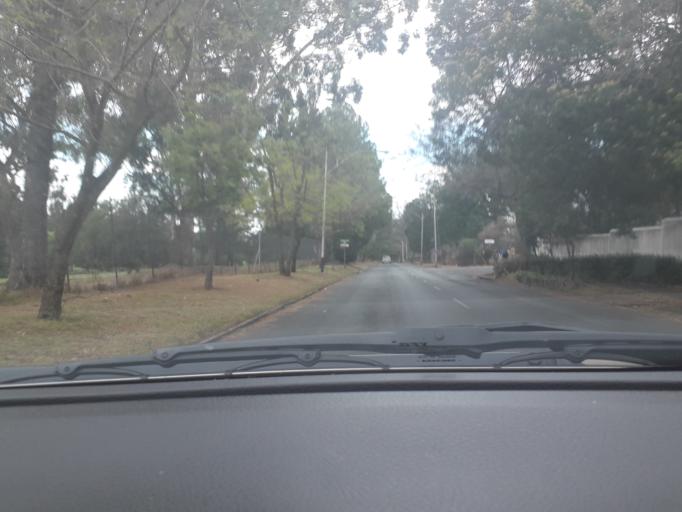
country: ZA
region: Gauteng
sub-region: City of Johannesburg Metropolitan Municipality
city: Johannesburg
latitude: -26.1578
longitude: 28.0203
